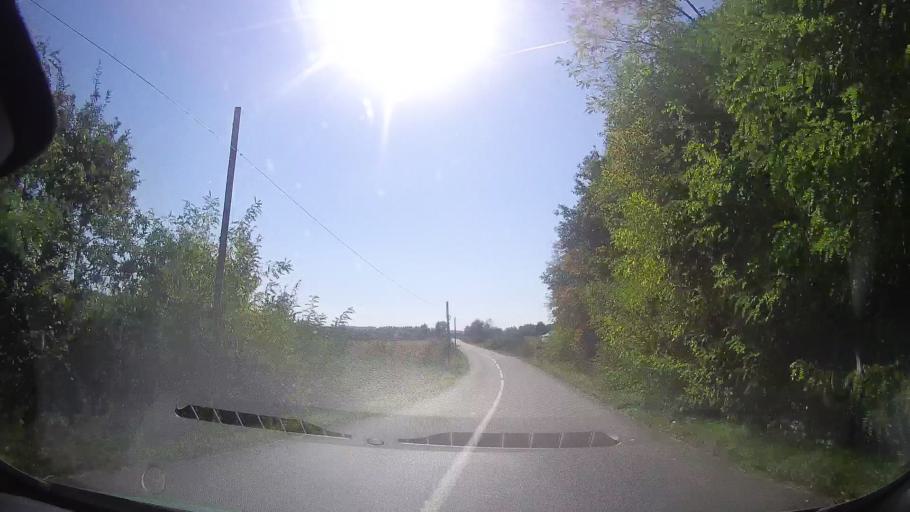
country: RO
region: Timis
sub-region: Comuna Ohaba Lunga
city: Ohaba Lunga
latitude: 45.8814
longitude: 21.9643
